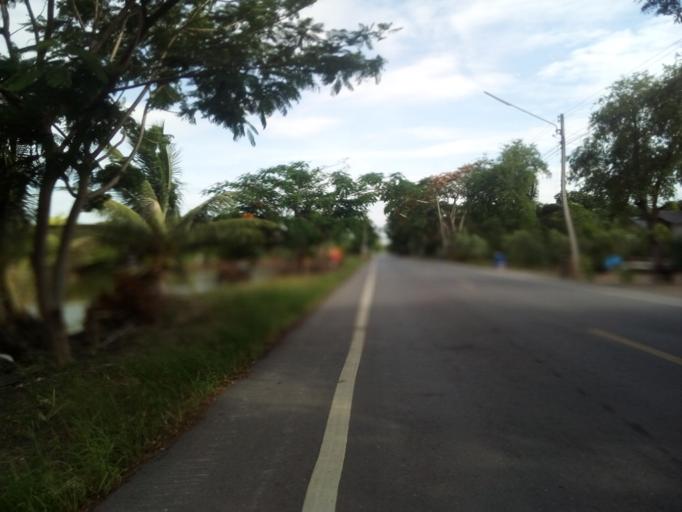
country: TH
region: Pathum Thani
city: Nong Suea
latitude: 14.0944
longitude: 100.8461
